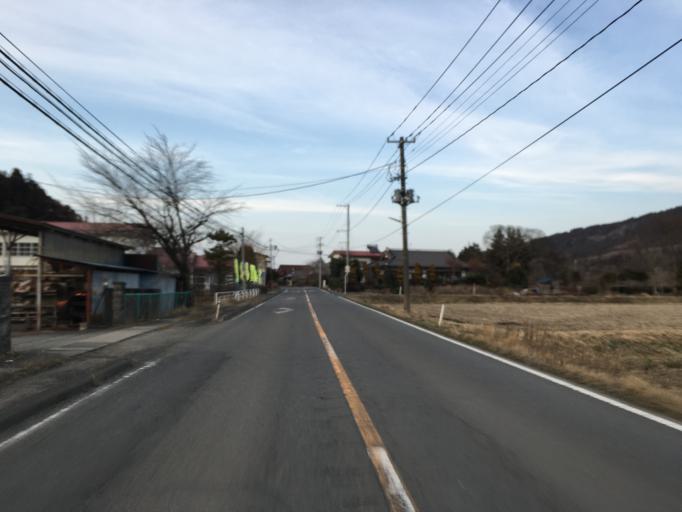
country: JP
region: Ibaraki
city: Daigo
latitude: 36.9285
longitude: 140.4087
